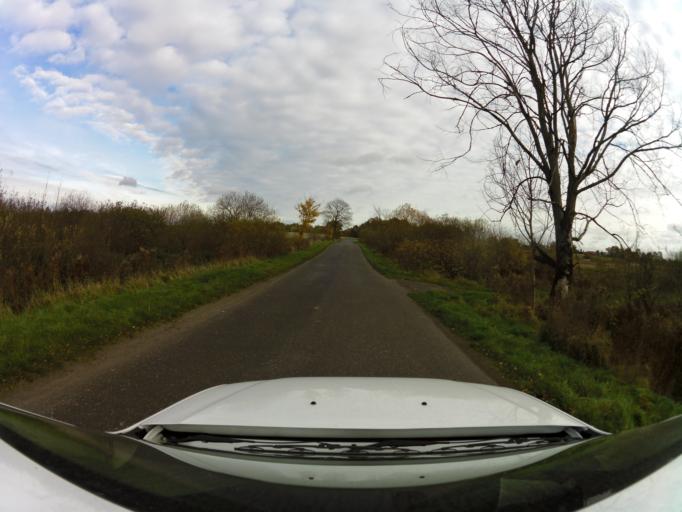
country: PL
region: West Pomeranian Voivodeship
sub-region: Powiat gryficki
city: Cerkwica
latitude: 54.0098
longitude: 15.1671
